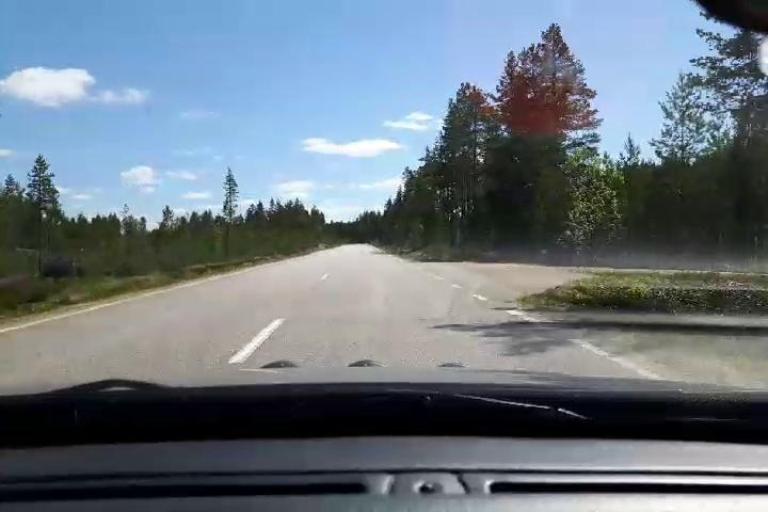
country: SE
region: Vaesternorrland
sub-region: Ange Kommun
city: Ange
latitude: 62.0631
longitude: 15.1117
